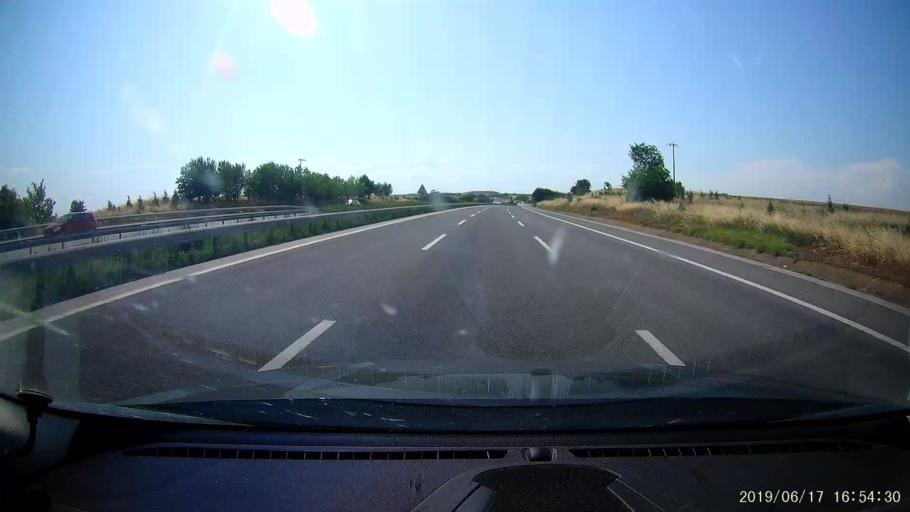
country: TR
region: Kirklareli
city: Inece
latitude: 41.5740
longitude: 26.9941
